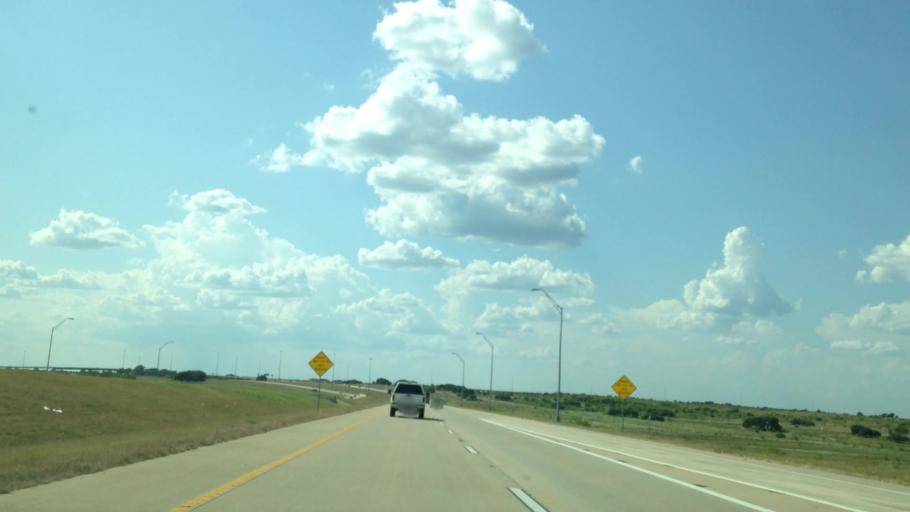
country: US
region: Texas
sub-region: Travis County
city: Onion Creek
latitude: 30.1049
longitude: -97.7861
